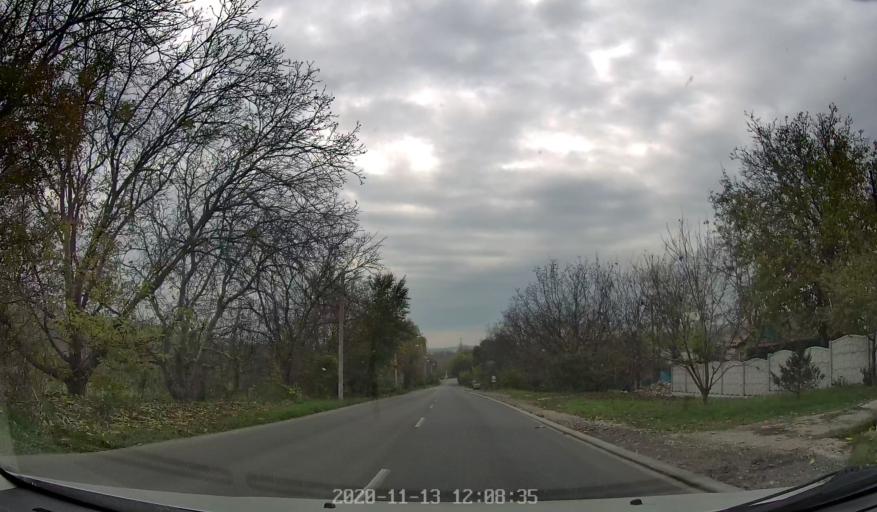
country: MD
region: Chisinau
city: Chisinau
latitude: 46.9646
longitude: 28.8345
